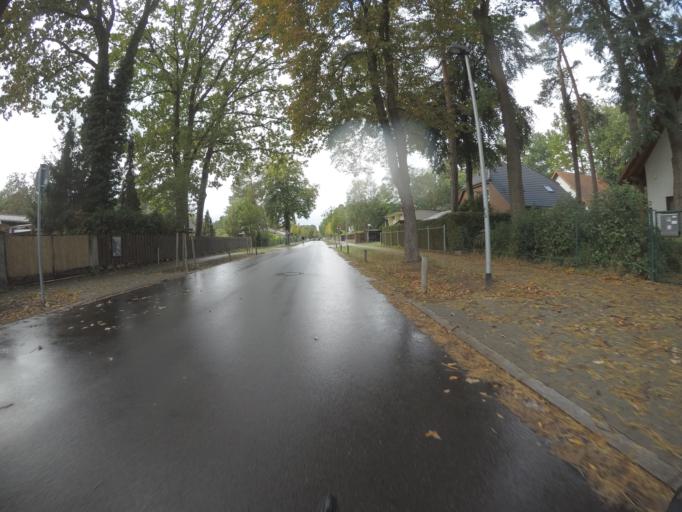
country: DE
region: Berlin
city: Blankenfelde
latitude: 52.6478
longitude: 13.3794
